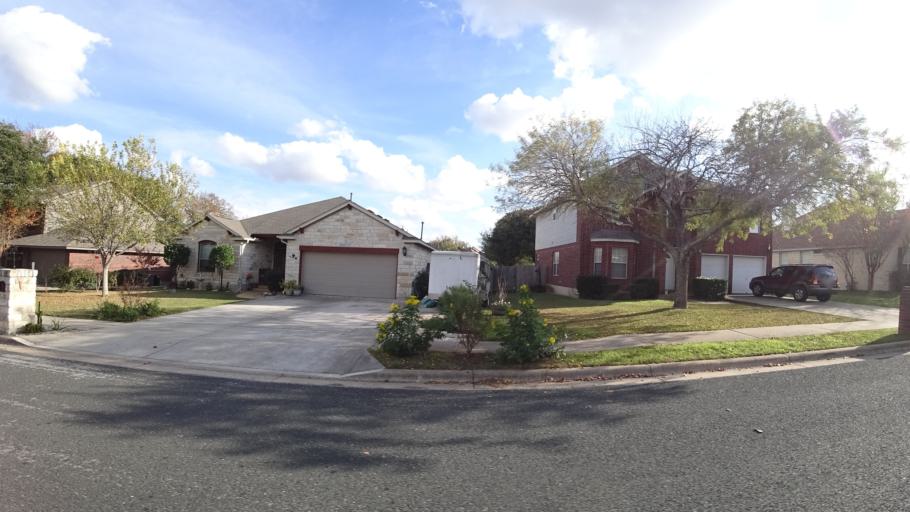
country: US
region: Texas
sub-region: Williamson County
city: Brushy Creek
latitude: 30.5105
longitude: -97.7253
